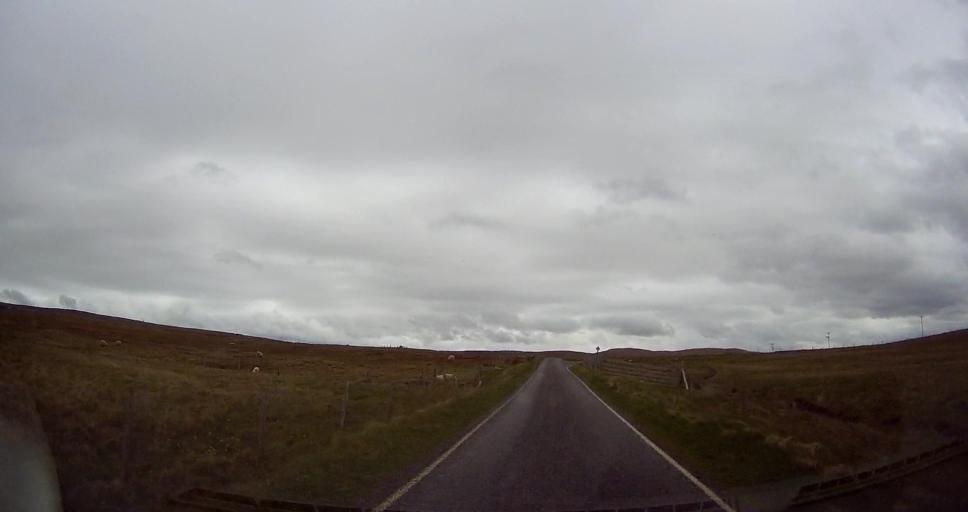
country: GB
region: Scotland
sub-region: Shetland Islands
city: Lerwick
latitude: 60.4865
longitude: -1.4858
